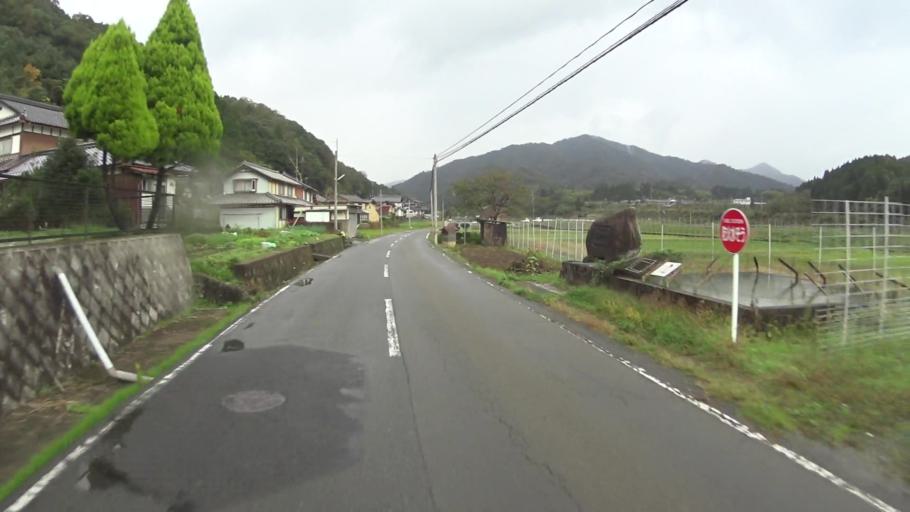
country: JP
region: Kyoto
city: Fukuchiyama
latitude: 35.4142
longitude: 135.1527
